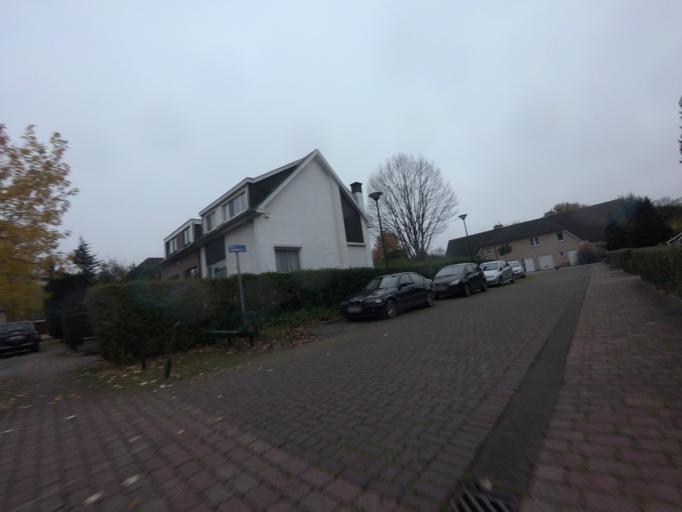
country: BE
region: Flanders
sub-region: Provincie Vlaams-Brabant
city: Diegem
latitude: 50.8629
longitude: 4.4340
